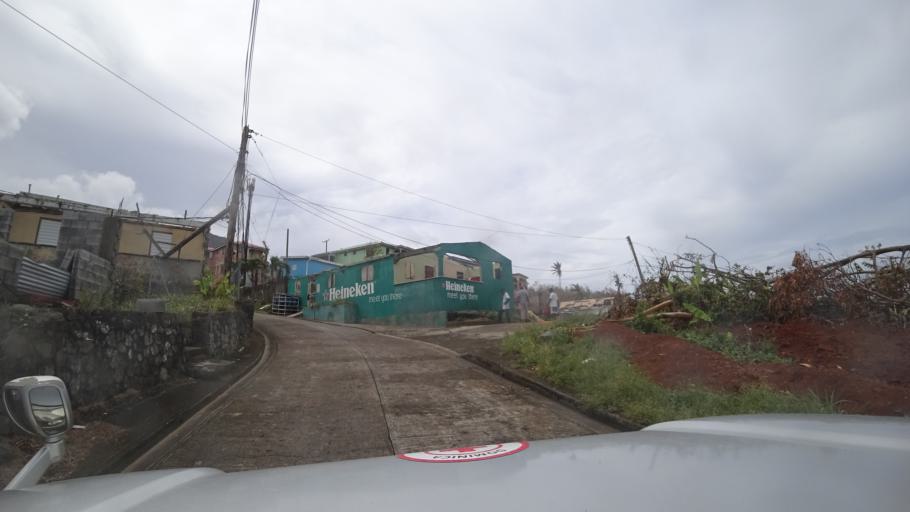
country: DM
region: Saint Andrew
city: Calibishie
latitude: 15.6141
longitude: -61.4051
